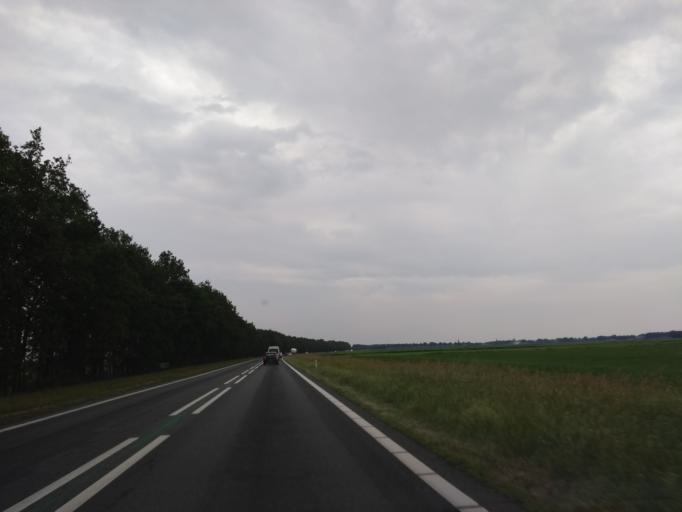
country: NL
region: Overijssel
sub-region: Gemeente Twenterand
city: Westerhaar-Vriezenveensewijk
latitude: 52.4870
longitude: 6.6028
